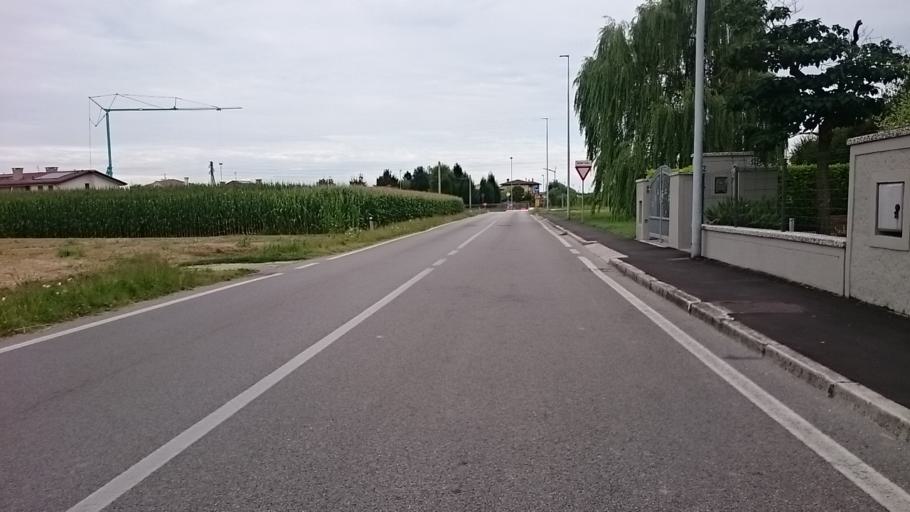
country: IT
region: Veneto
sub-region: Provincia di Padova
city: Masera di Padova
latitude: 45.3353
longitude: 11.8681
